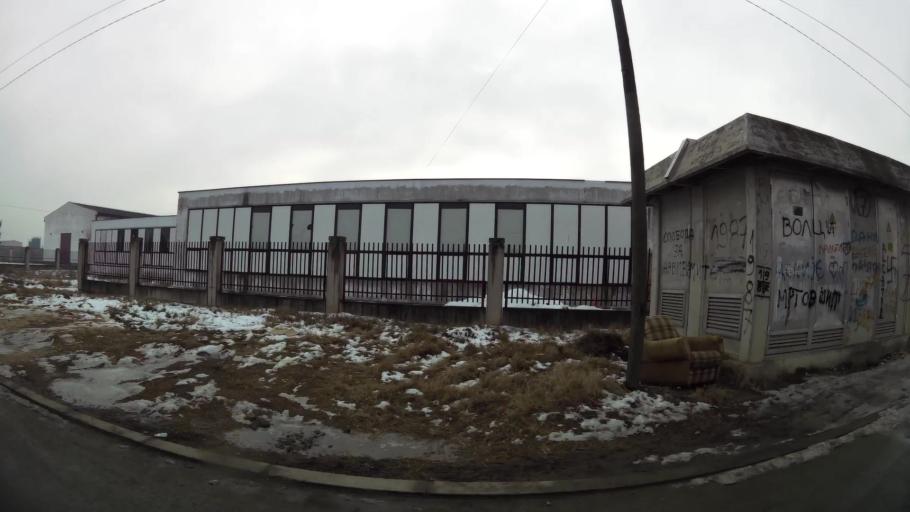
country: MK
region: Ilinden
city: Ilinden
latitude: 41.9918
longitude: 21.5769
